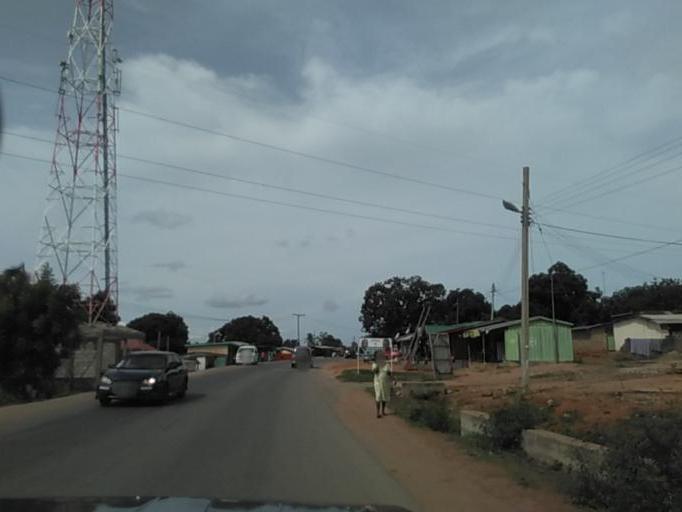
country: GH
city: Akropong
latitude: 6.2319
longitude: 0.0919
